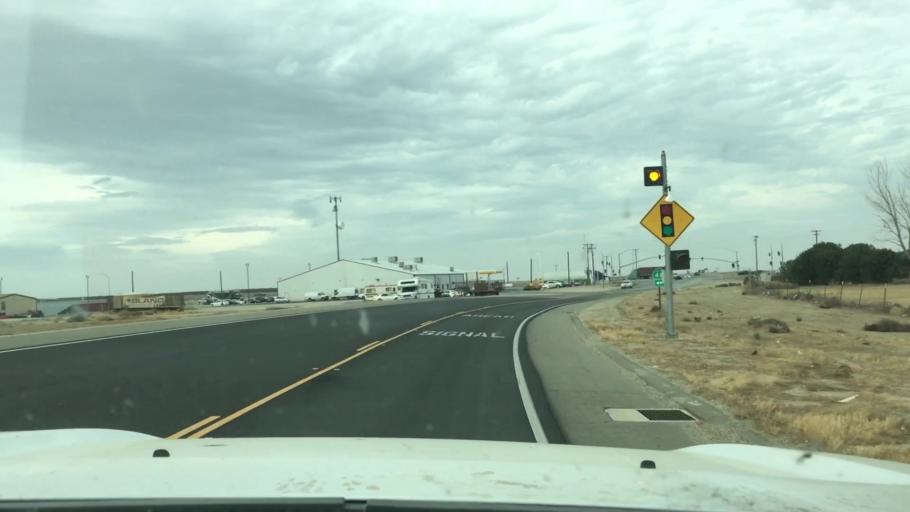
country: US
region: California
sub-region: Kern County
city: Lost Hills
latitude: 35.6123
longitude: -119.8674
